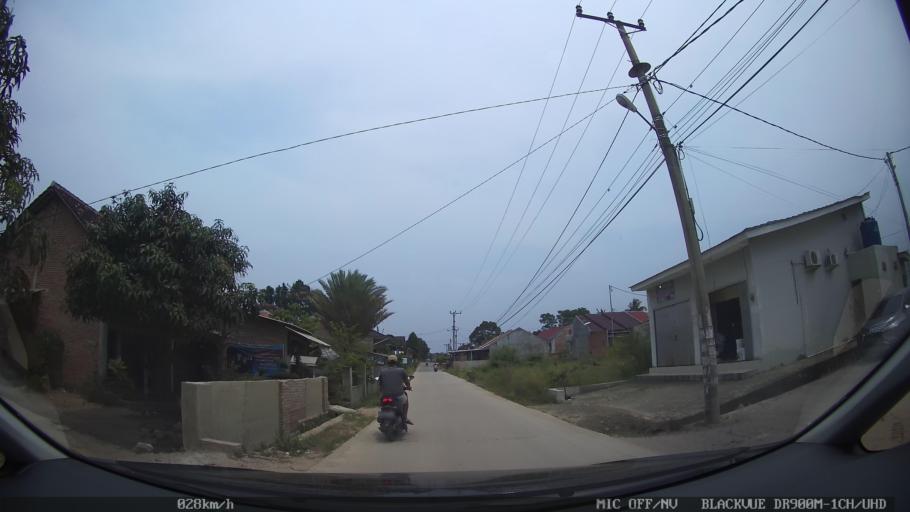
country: ID
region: Lampung
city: Kedaton
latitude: -5.3950
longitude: 105.3182
